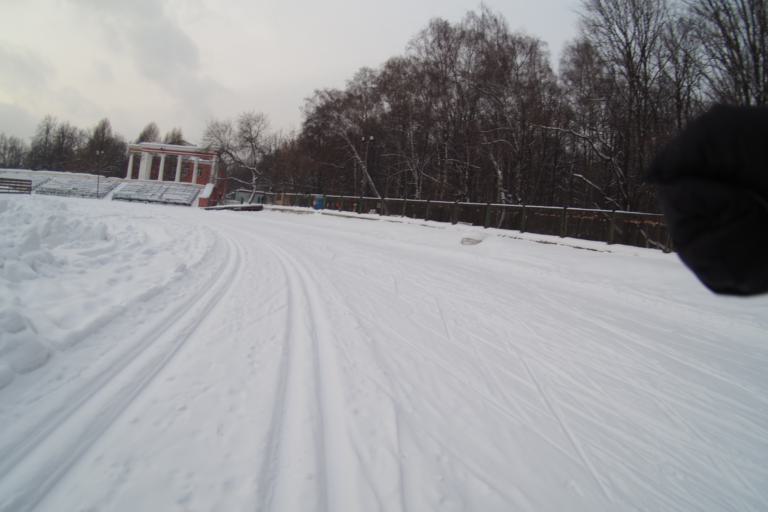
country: RU
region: Moscow
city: Ryazanskiy
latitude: 55.7648
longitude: 37.7749
